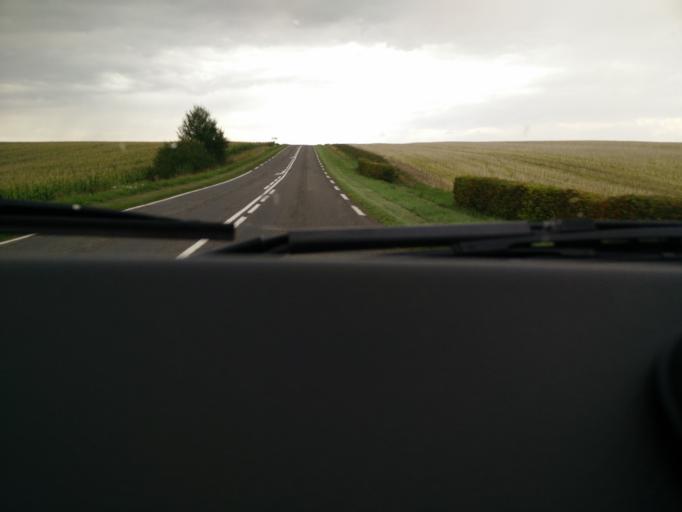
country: FR
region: Picardie
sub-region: Departement de l'Aisne
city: Saint-Michel
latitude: 49.8749
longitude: 4.1590
